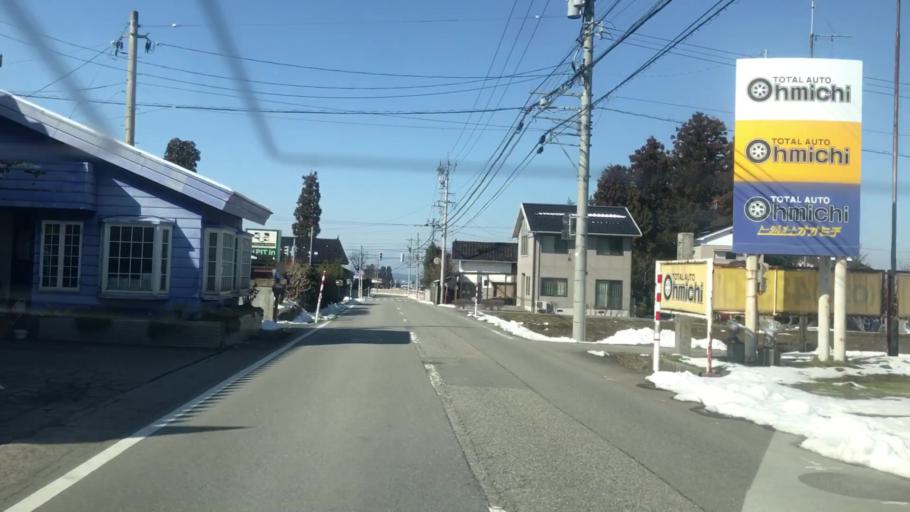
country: JP
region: Toyama
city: Toyama-shi
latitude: 36.6268
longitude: 137.2759
